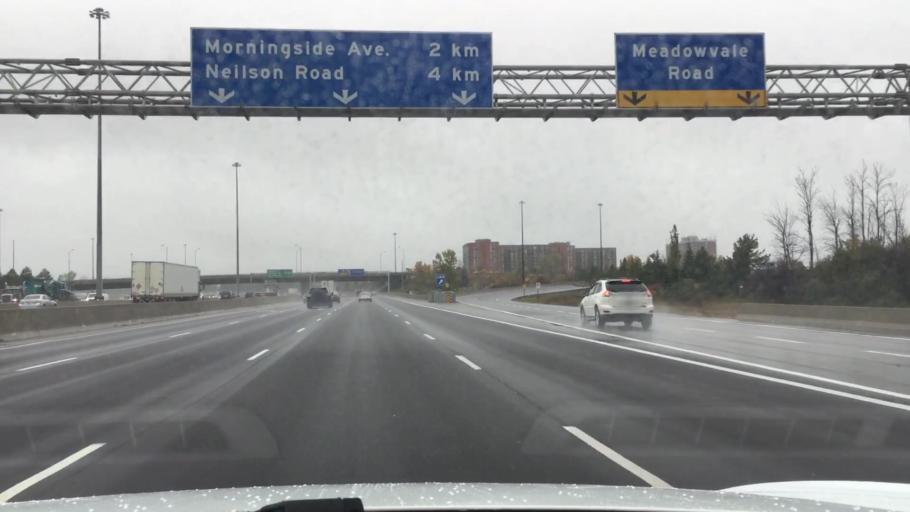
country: CA
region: Ontario
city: Scarborough
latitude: 43.7986
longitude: -79.1622
